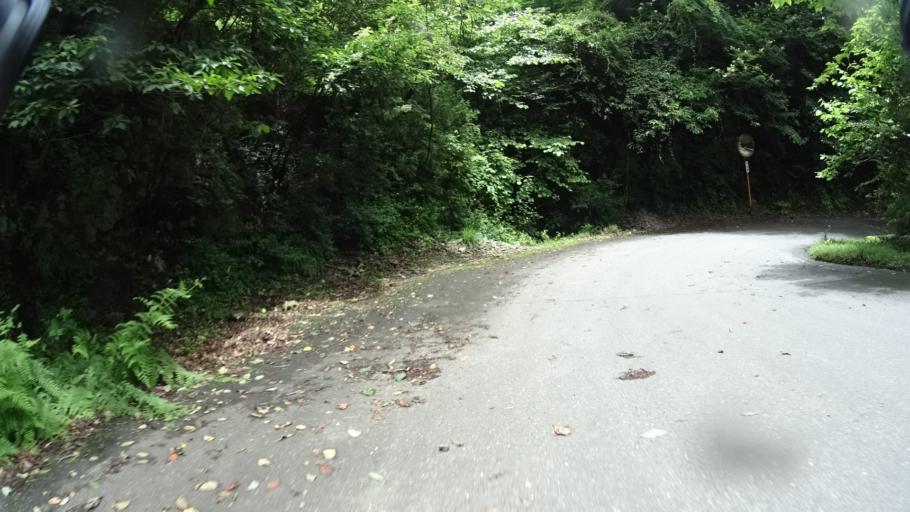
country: JP
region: Saitama
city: Chichibu
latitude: 35.8913
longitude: 139.1356
